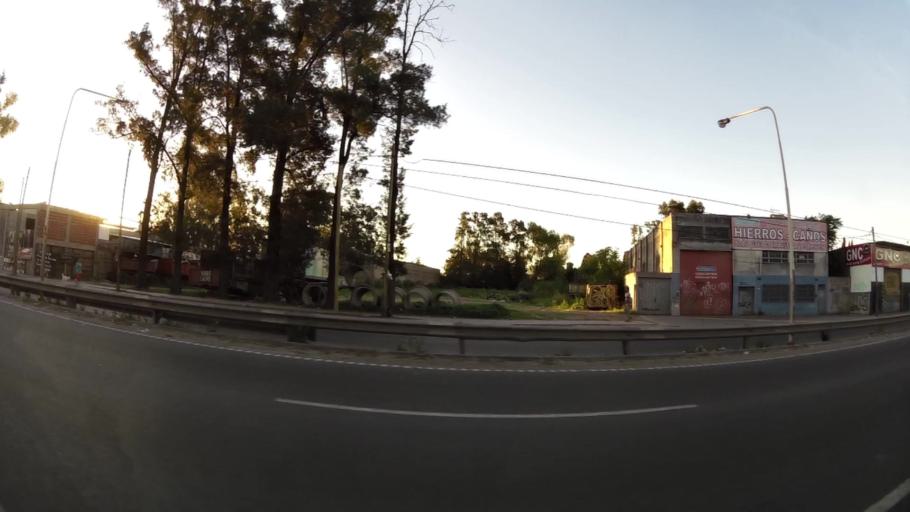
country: AR
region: Buenos Aires
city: Pontevedra
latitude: -34.7848
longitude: -58.6264
